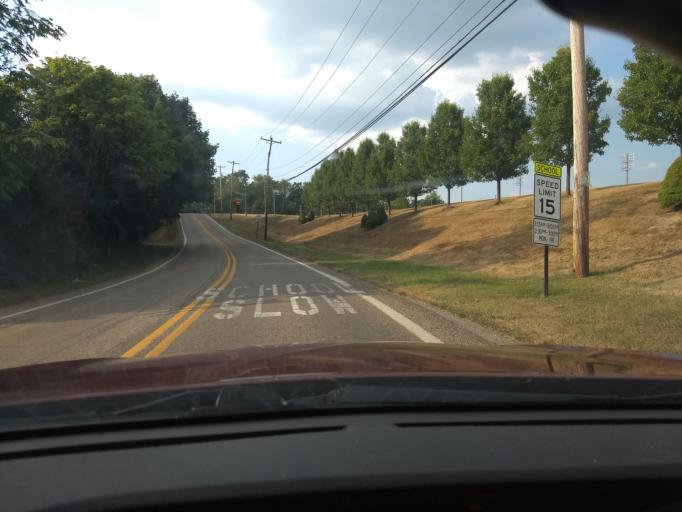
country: US
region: Pennsylvania
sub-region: Allegheny County
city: Russellton
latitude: 40.6168
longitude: -79.8529
